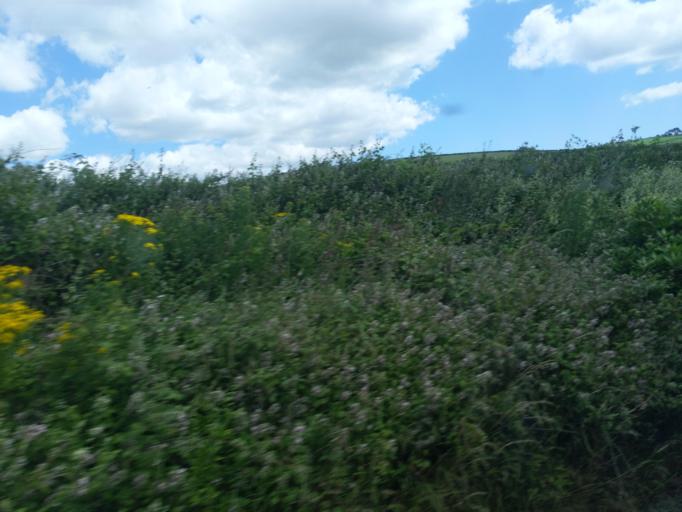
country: GB
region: England
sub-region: Cornwall
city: Par
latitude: 50.3733
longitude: -4.6821
